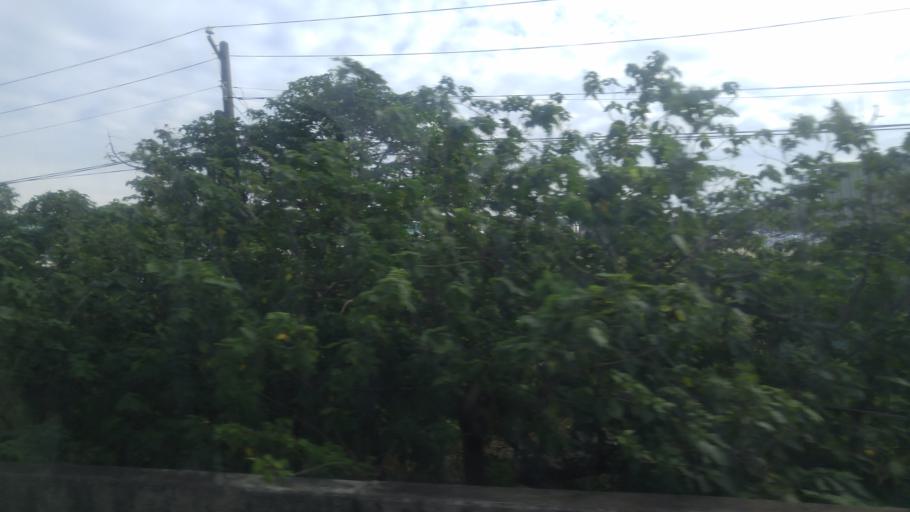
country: TW
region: Taiwan
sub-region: Hsinchu
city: Zhubei
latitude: 24.8946
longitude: 121.1300
